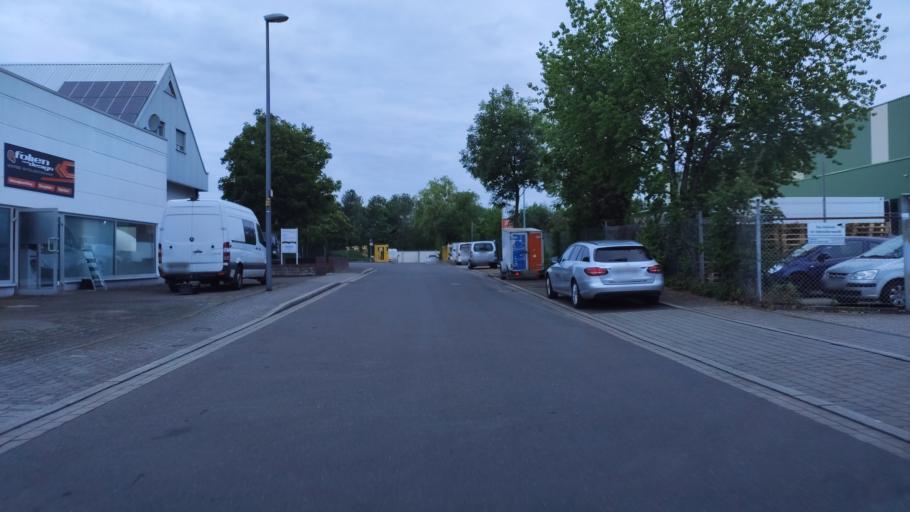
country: DE
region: North Rhine-Westphalia
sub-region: Regierungsbezirk Dusseldorf
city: Dormagen
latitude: 51.0953
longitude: 6.8184
